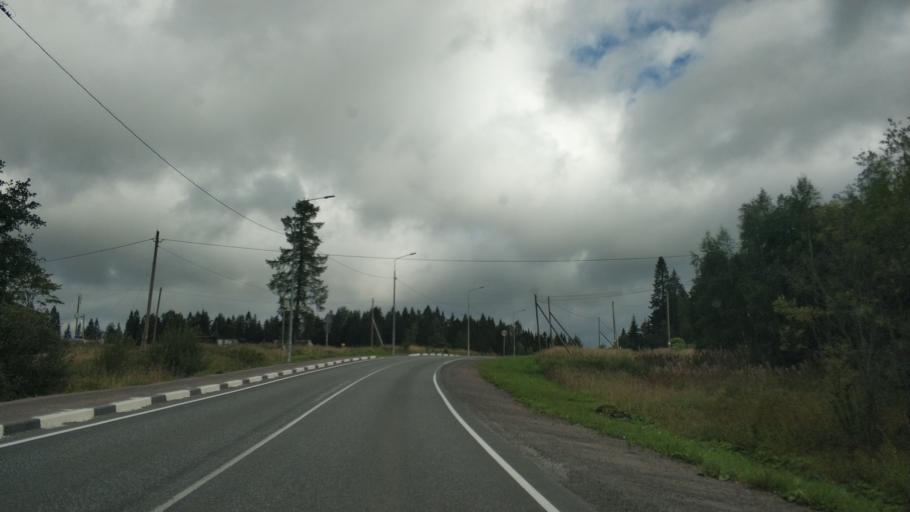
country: RU
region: Republic of Karelia
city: Khelyulya
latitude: 61.7671
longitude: 30.6542
